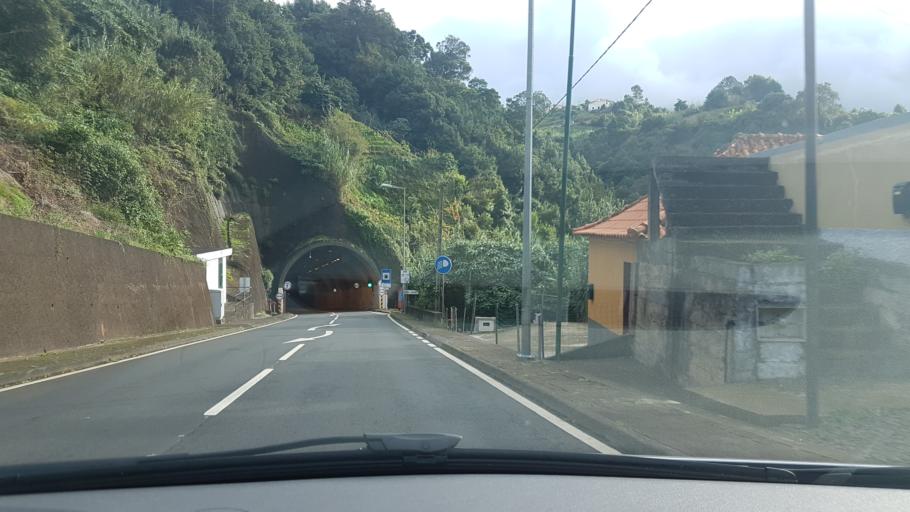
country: PT
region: Madeira
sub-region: Santana
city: Santana
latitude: 32.8192
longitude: -16.8911
